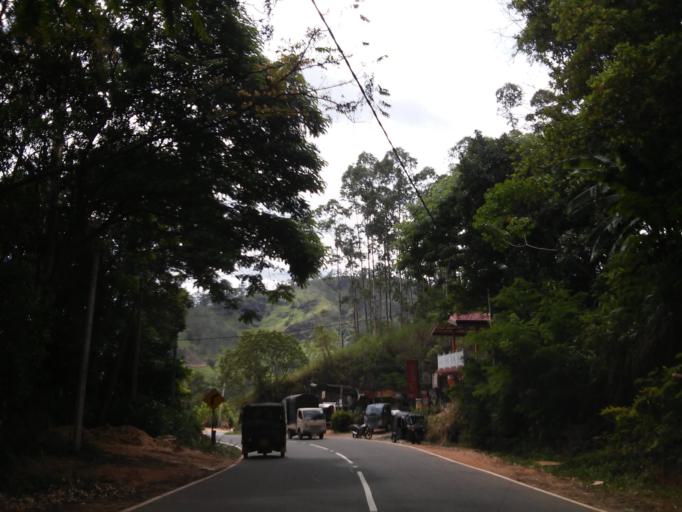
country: LK
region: Uva
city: Haputale
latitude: 6.8712
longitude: 80.9504
